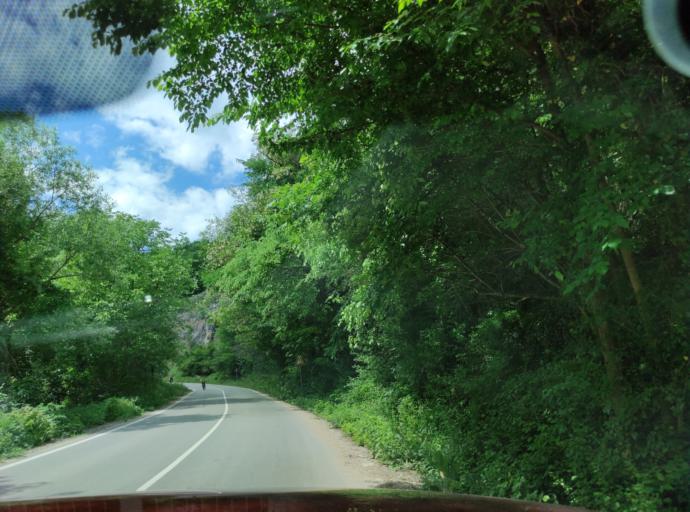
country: BG
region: Montana
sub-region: Obshtina Chiprovtsi
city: Chiprovtsi
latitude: 43.4412
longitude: 22.9350
